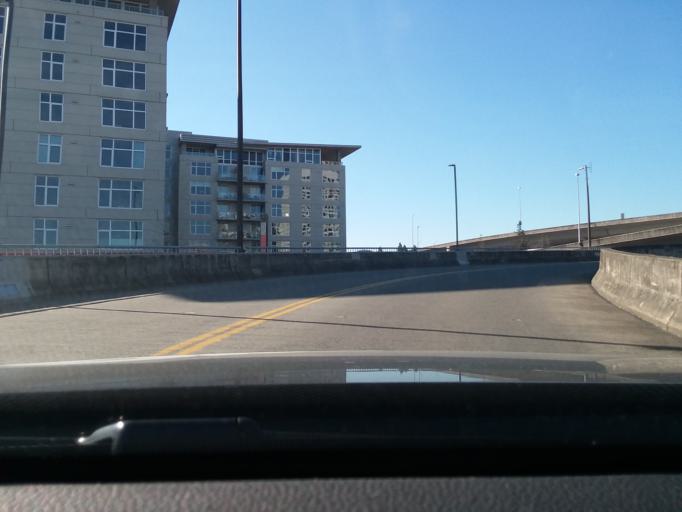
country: US
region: Washington
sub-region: Pierce County
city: Tacoma
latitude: 47.2500
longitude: -122.4347
